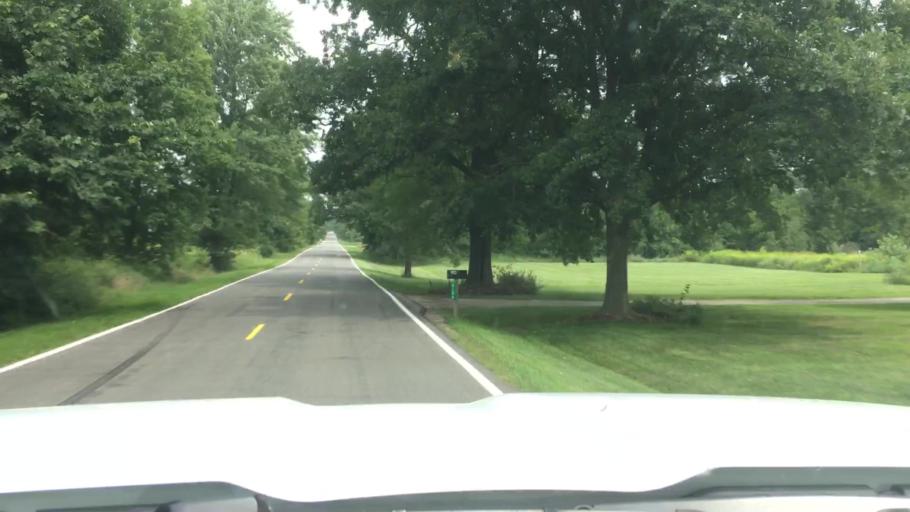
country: US
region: Michigan
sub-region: Ingham County
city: Webberville
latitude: 42.6774
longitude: -84.1893
